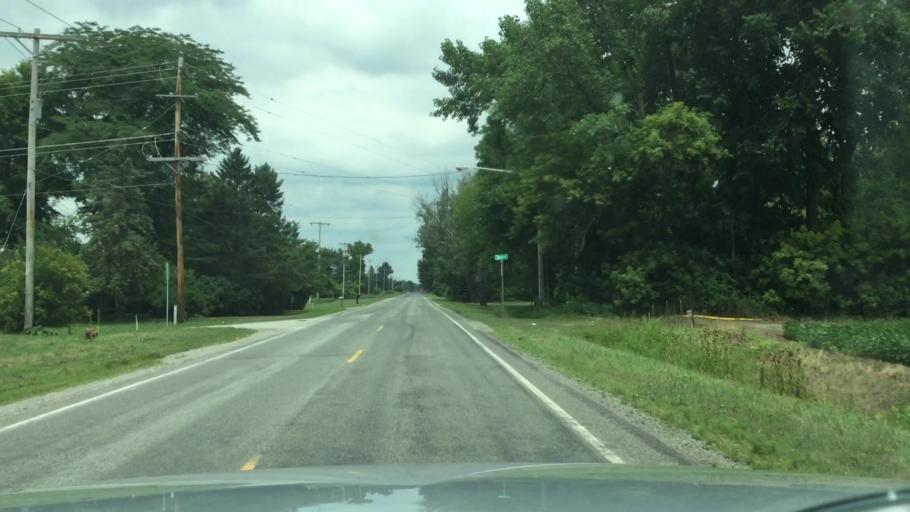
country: US
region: Michigan
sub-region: Saginaw County
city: Burt
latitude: 43.2870
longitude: -83.8944
